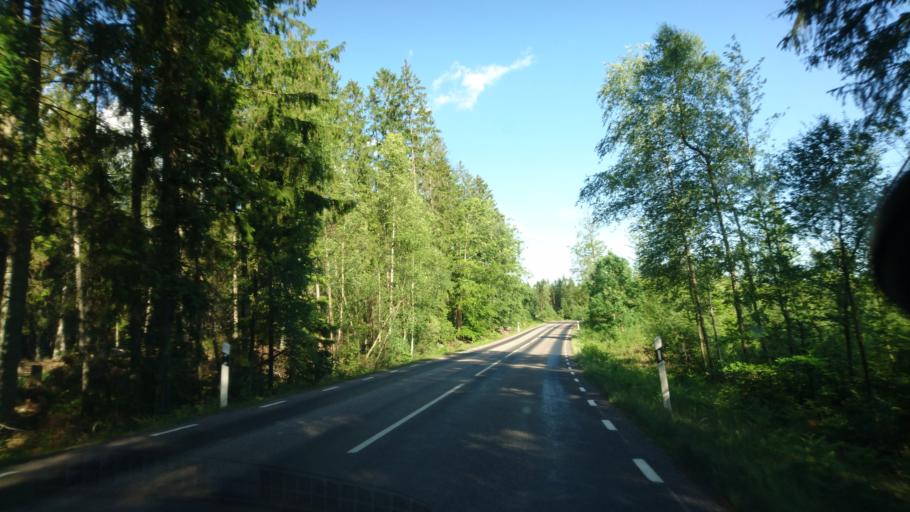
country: SE
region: Skane
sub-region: Osby Kommun
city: Lonsboda
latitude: 56.3899
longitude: 14.3655
